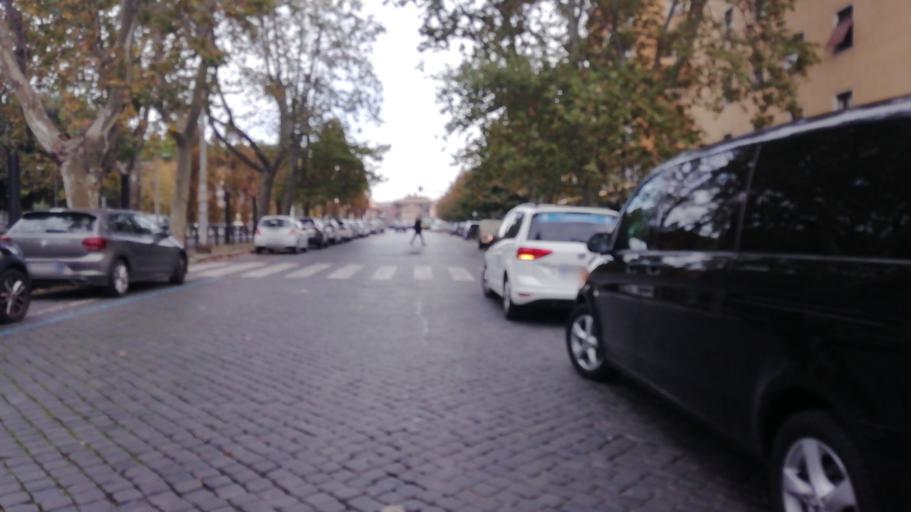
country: IT
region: Latium
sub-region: Citta metropolitana di Roma Capitale
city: Rome
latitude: 41.8784
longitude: 12.4826
